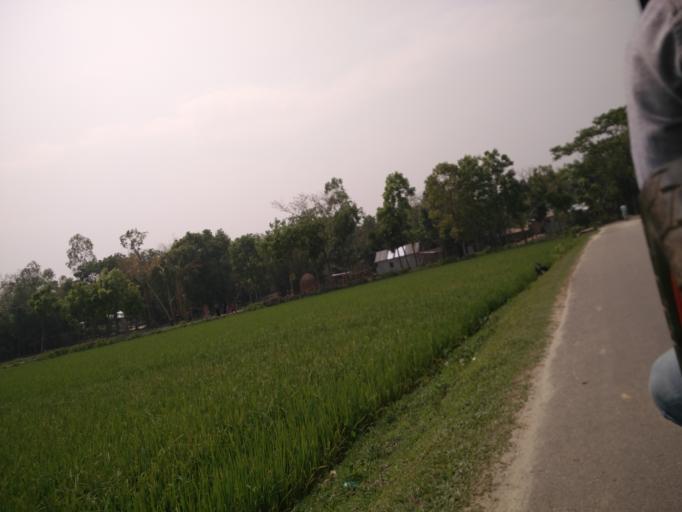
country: BD
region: Dhaka
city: Muktagacha
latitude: 24.8889
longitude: 90.2692
